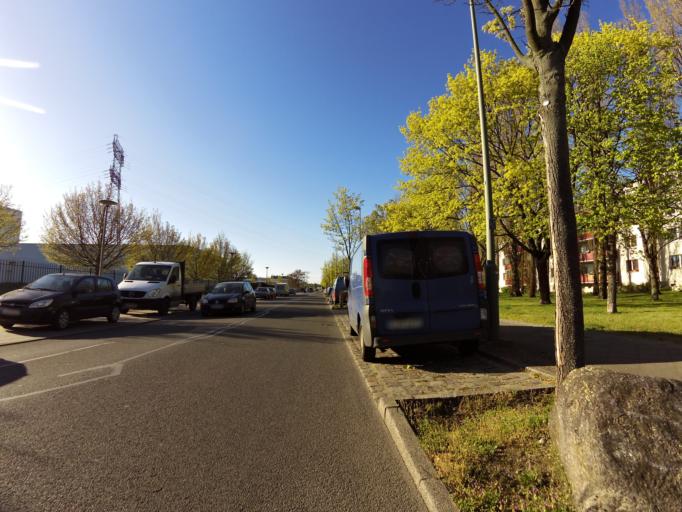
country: DE
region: Berlin
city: Niederschoneweide
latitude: 52.4670
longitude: 13.5058
